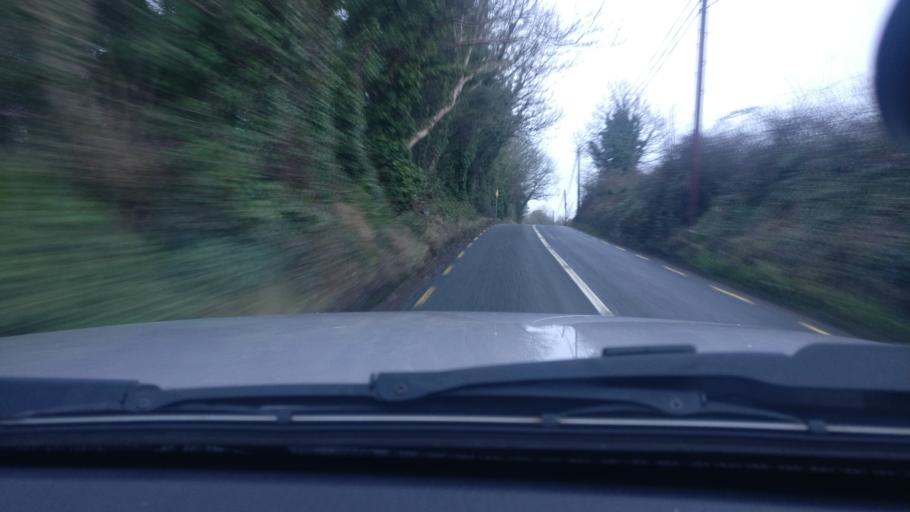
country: IE
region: Connaught
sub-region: County Galway
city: Loughrea
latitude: 53.1667
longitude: -8.5214
